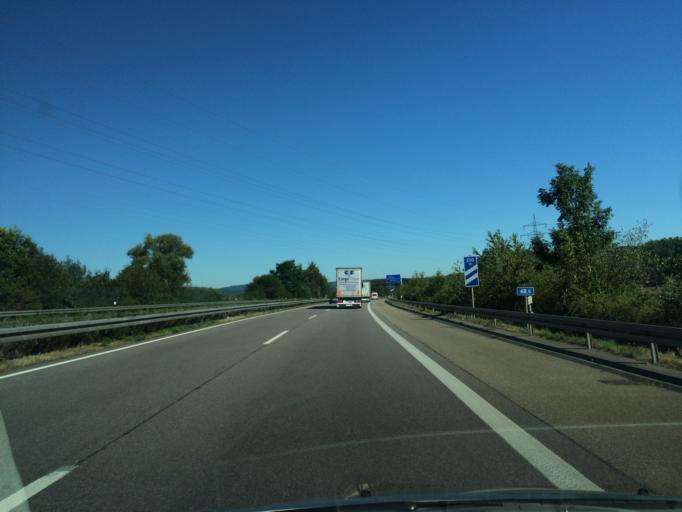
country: DE
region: Saarland
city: Merzig
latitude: 49.4352
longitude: 6.6264
